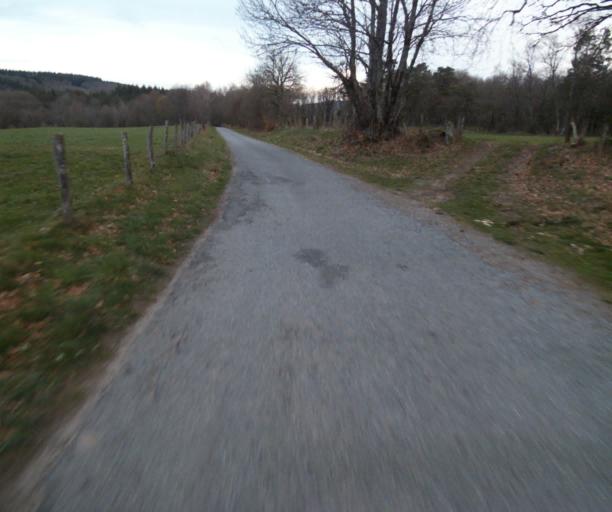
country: FR
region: Limousin
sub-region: Departement de la Correze
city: Correze
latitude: 45.4407
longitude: 1.8387
